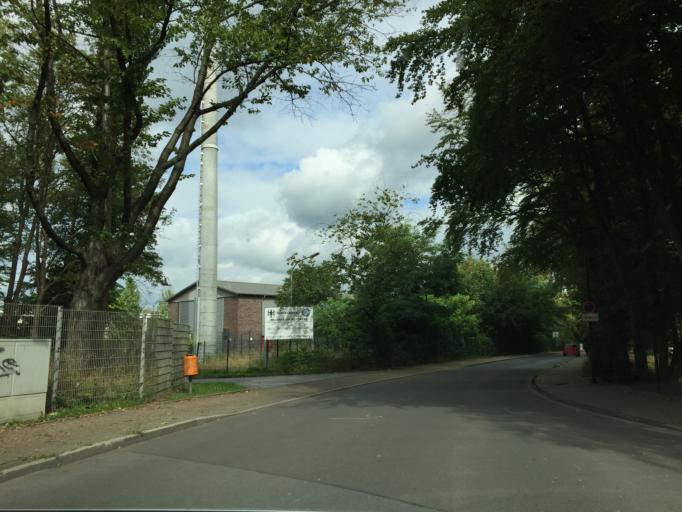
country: DE
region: North Rhine-Westphalia
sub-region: Regierungsbezirk Dusseldorf
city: Heiligenhaus
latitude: 51.3297
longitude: 6.9544
